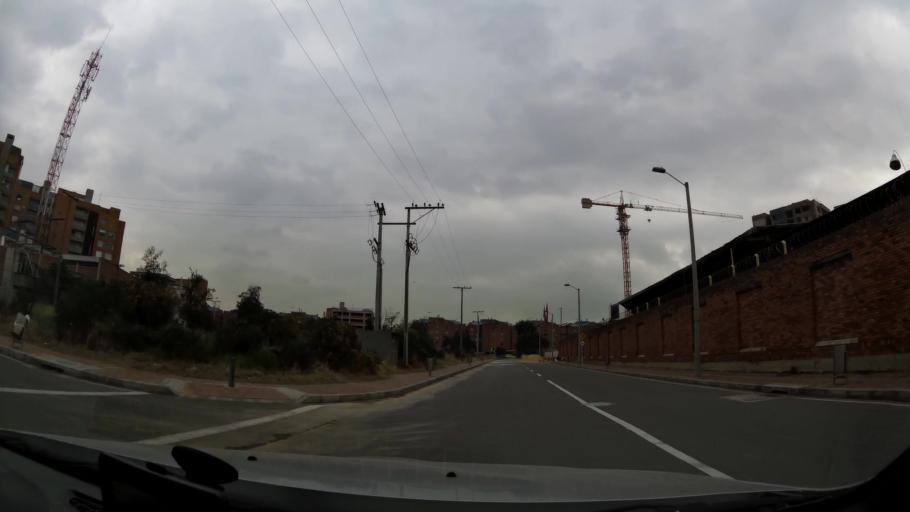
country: CO
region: Bogota D.C.
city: Bogota
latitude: 4.6633
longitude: -74.1125
